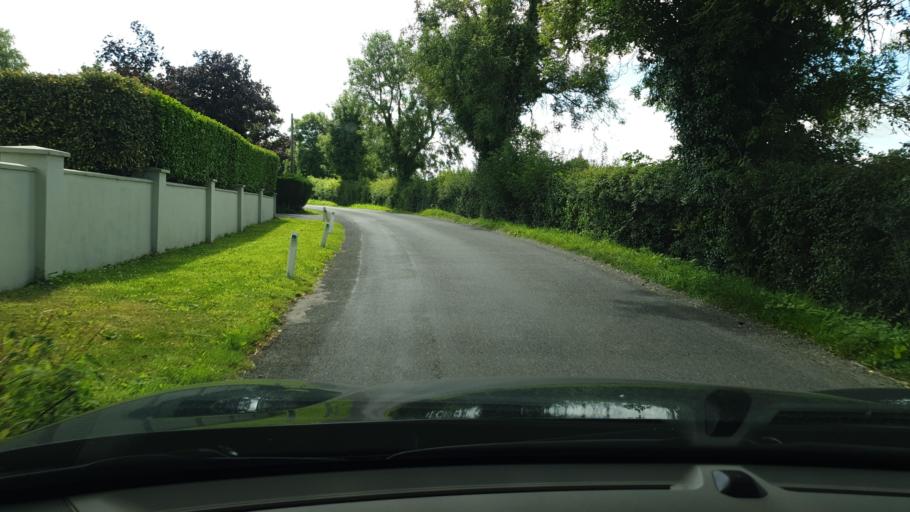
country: IE
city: Confey
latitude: 53.4021
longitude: -6.4928
